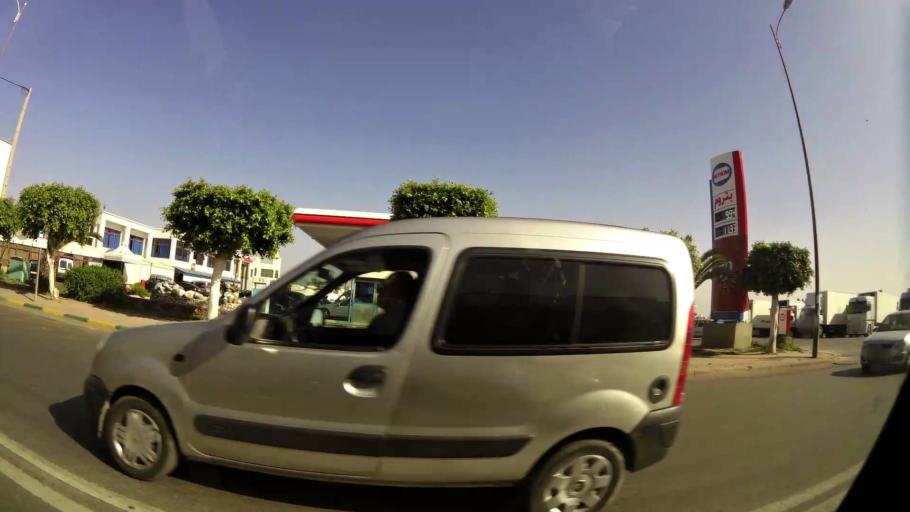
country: MA
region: Souss-Massa-Draa
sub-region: Inezgane-Ait Mellou
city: Inezgane
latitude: 30.3820
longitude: -9.5214
